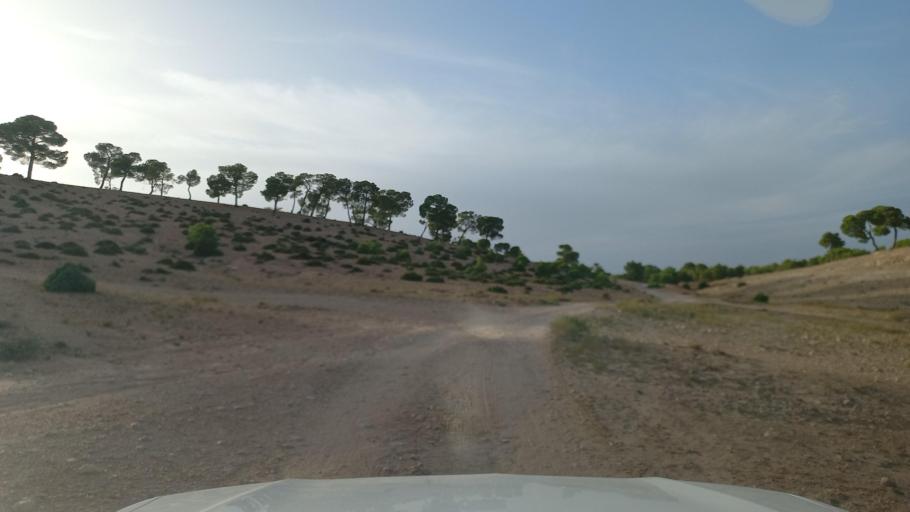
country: TN
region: Al Qasrayn
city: Sbiba
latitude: 35.4102
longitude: 8.8982
